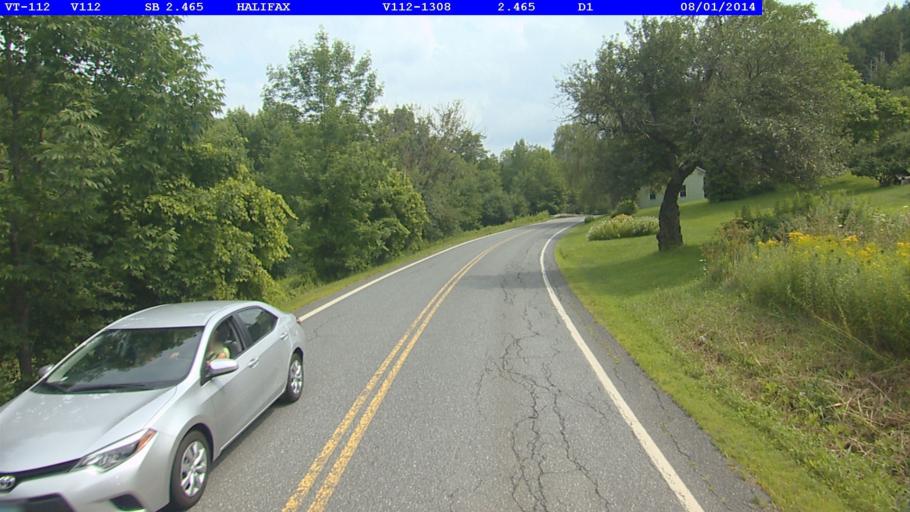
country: US
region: Massachusetts
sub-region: Franklin County
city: Colrain
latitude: 42.7551
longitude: -72.7567
